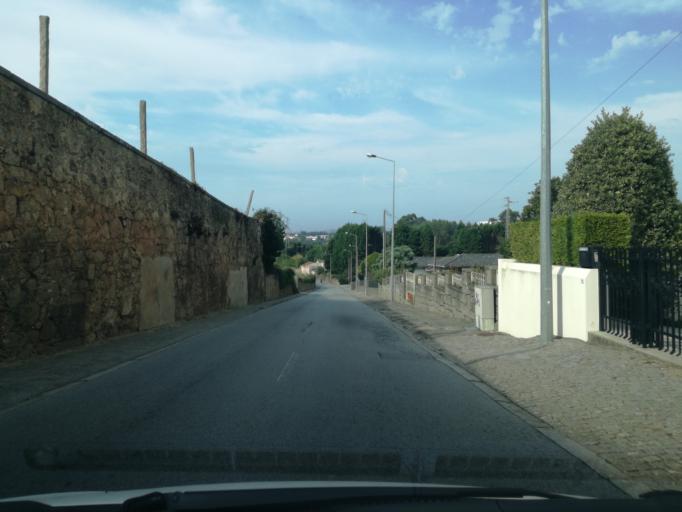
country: PT
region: Porto
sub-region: Vila Nova de Gaia
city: Arcozelo
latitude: 41.0530
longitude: -8.6267
